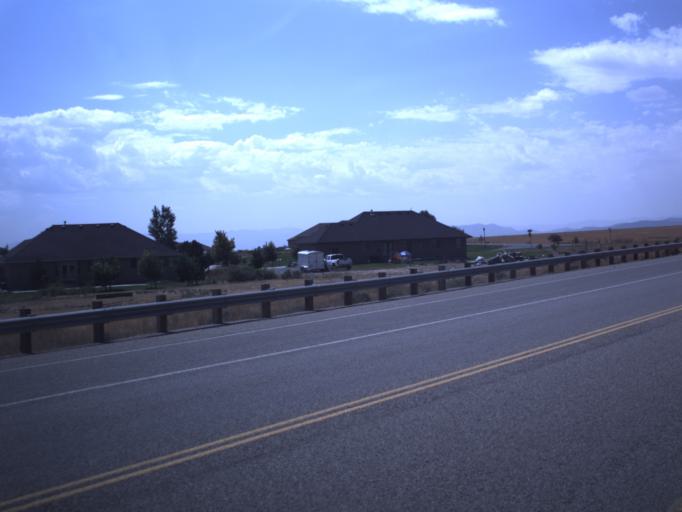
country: US
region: Utah
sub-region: Utah County
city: Eagle Mountain
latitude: 40.3731
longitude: -112.0194
